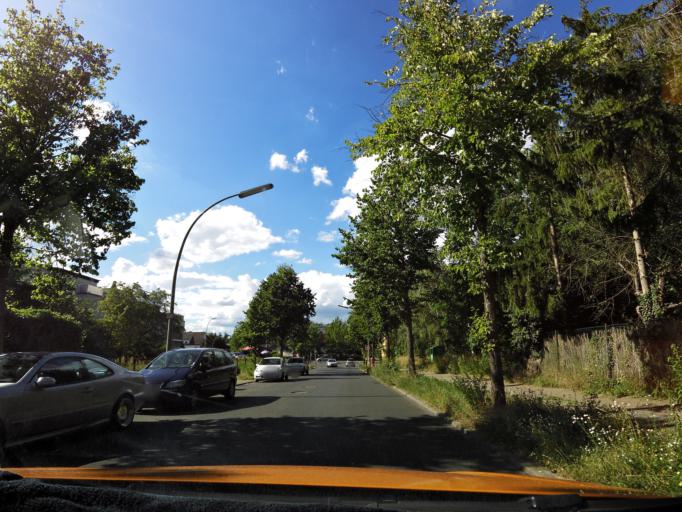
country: DE
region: Berlin
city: Lichtenrade
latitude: 52.3977
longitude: 13.3895
